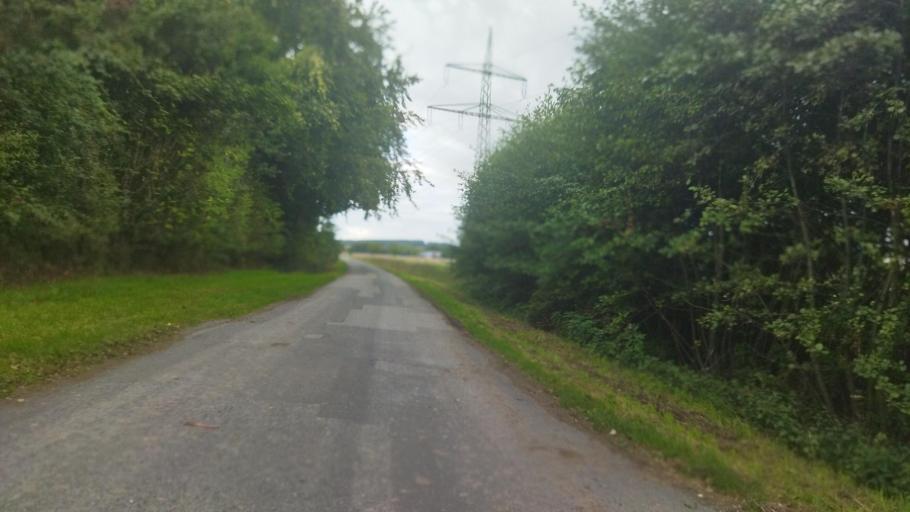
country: DE
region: North Rhine-Westphalia
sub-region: Regierungsbezirk Munster
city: Dulmen
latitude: 51.8873
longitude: 7.2649
